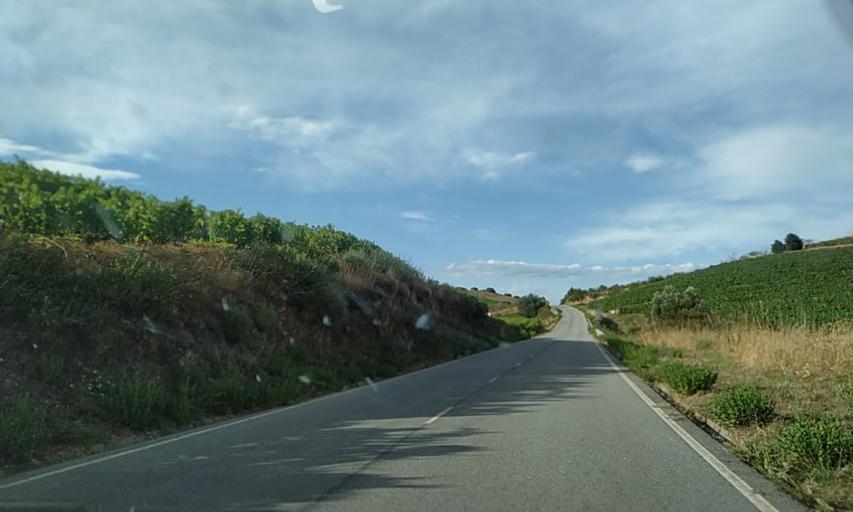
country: PT
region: Viseu
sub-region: Sao Joao da Pesqueira
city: Sao Joao da Pesqueira
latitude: 41.1354
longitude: -7.4382
